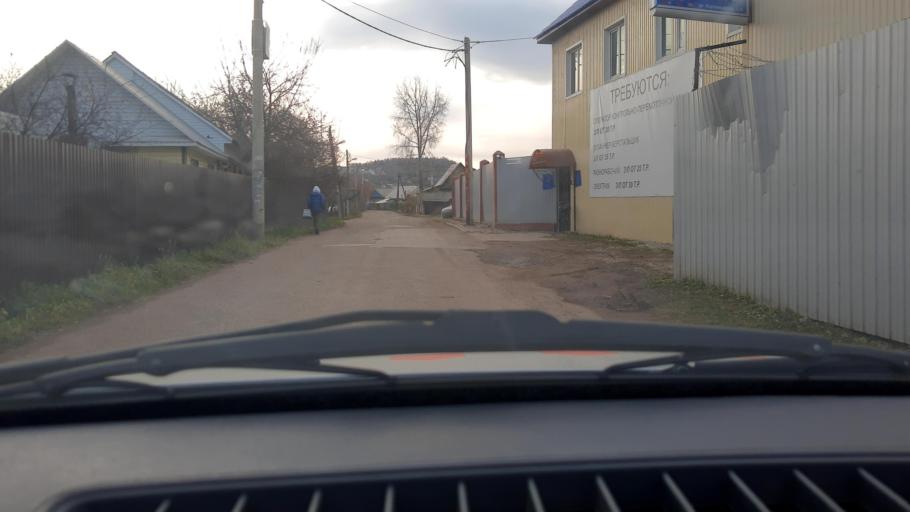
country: RU
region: Bashkortostan
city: Ufa
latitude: 54.7389
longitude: 55.9052
